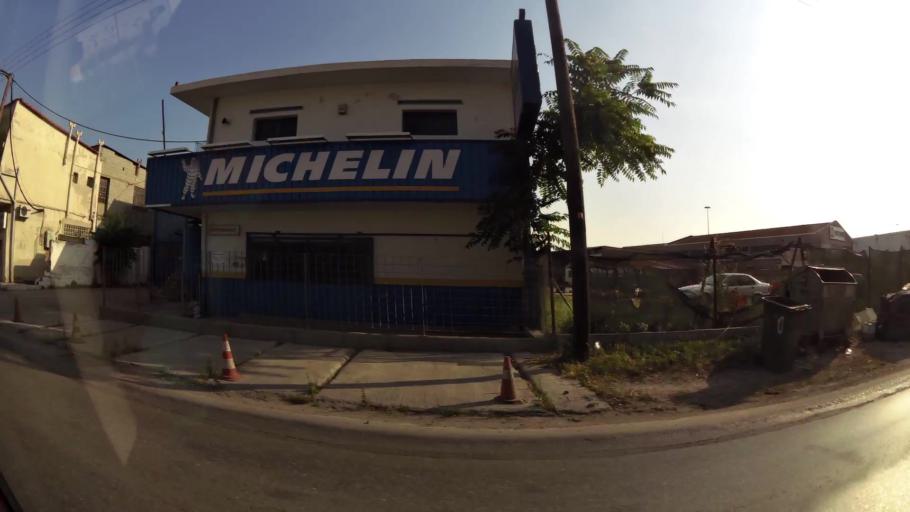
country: GR
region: Central Macedonia
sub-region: Nomos Thessalonikis
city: Diavata
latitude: 40.6743
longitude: 22.8783
